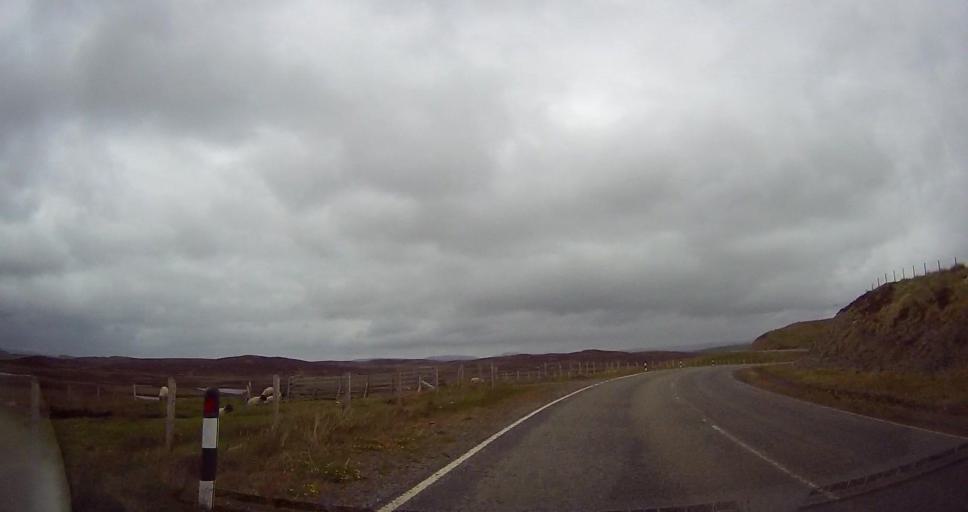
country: GB
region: Scotland
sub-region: Shetland Islands
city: Sandwick
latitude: 60.2589
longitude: -1.4918
